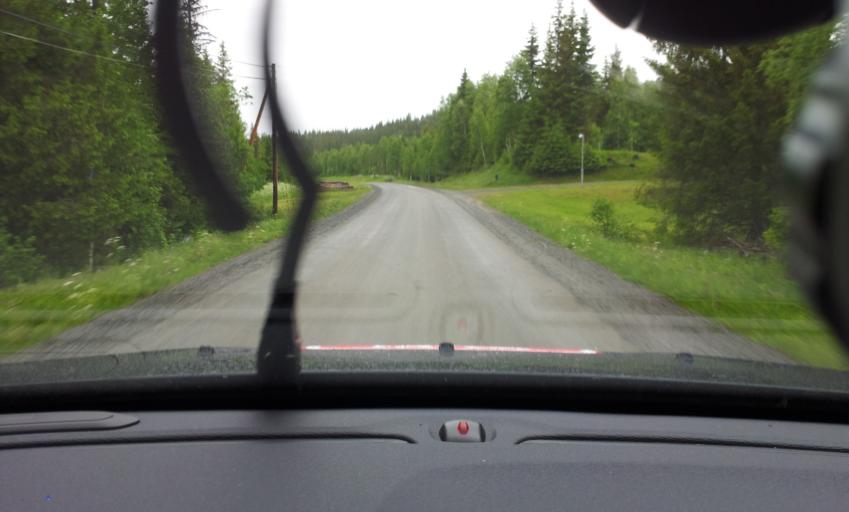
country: SE
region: Jaemtland
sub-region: Are Kommun
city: Are
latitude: 63.4815
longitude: 12.7957
